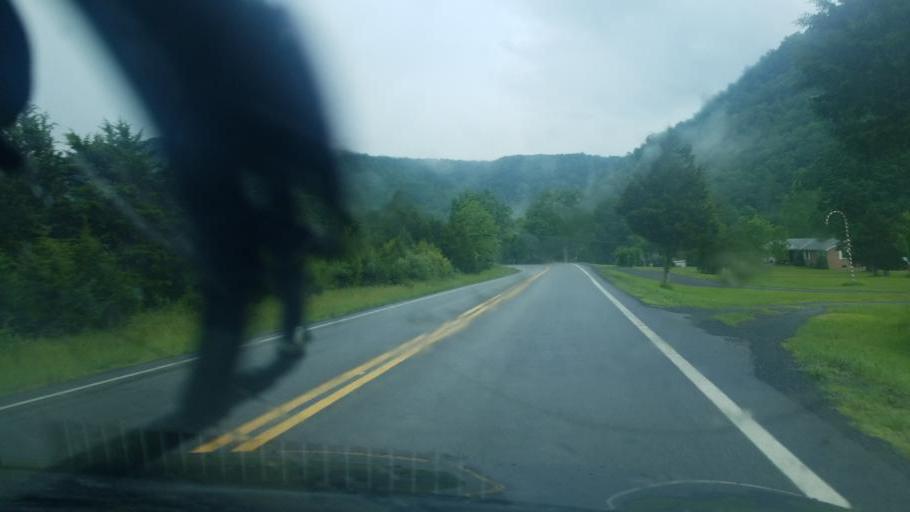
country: US
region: West Virginia
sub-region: Pendleton County
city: Franklin
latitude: 38.6708
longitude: -79.2851
